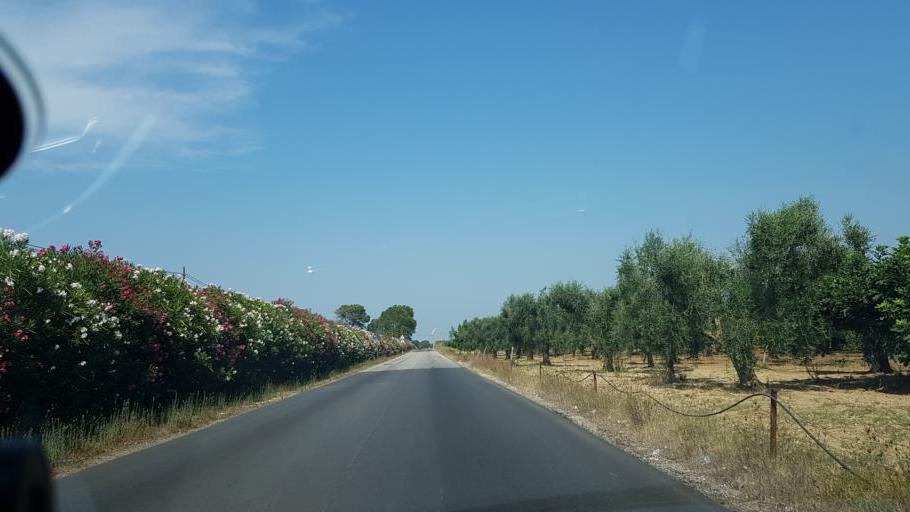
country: IT
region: Apulia
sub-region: Provincia di Brindisi
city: Torre Santa Susanna
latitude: 40.4991
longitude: 17.7648
